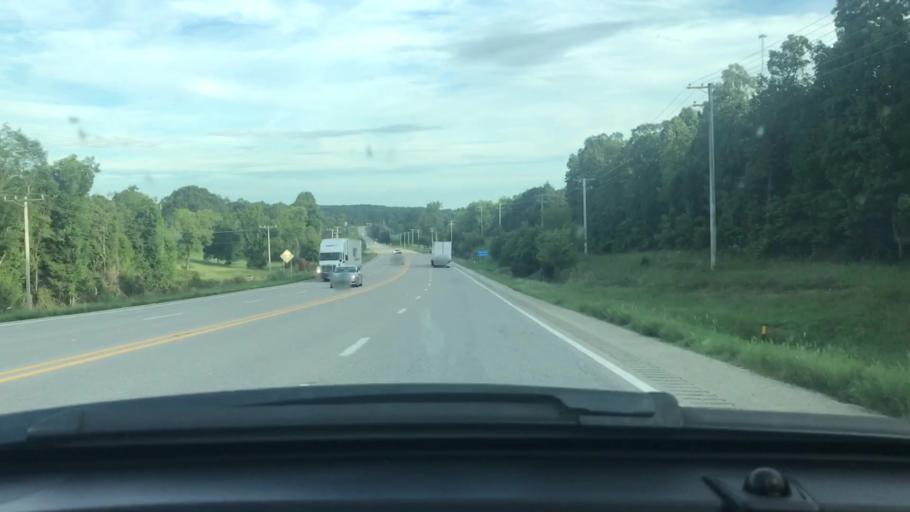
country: US
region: Arkansas
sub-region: Lawrence County
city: Hoxie
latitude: 36.1261
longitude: -91.1551
